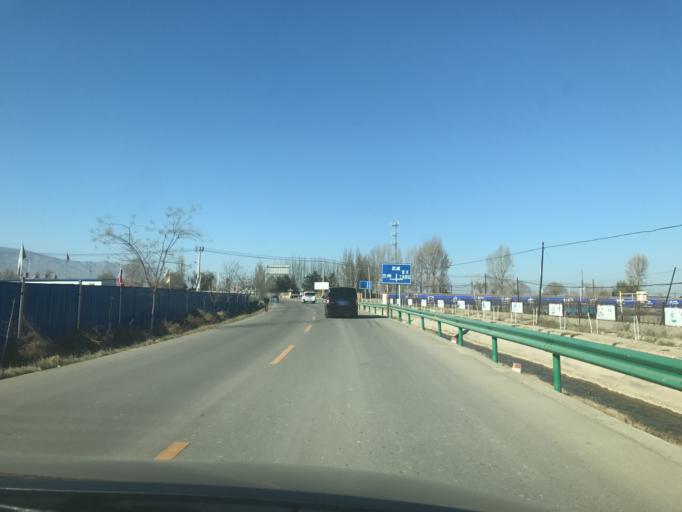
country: CN
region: Gansu Sheng
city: Gulang
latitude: 37.6771
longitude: 102.8369
